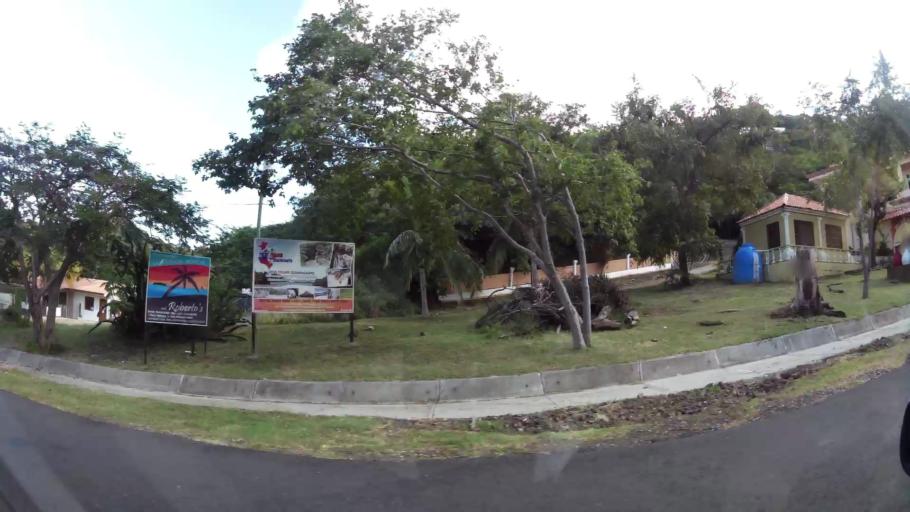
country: CR
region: Guanacaste
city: Sardinal
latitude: 10.5655
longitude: -85.6782
